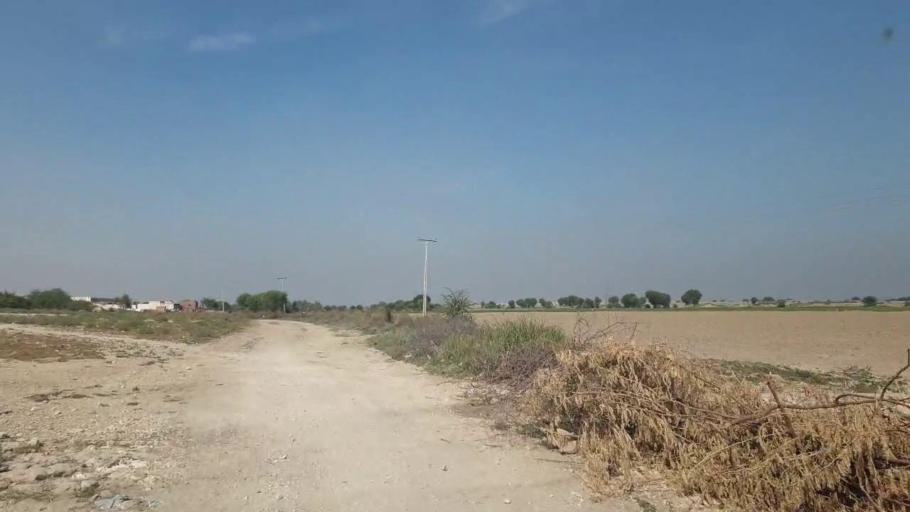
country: PK
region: Sindh
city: Hala
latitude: 25.7629
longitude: 68.2946
